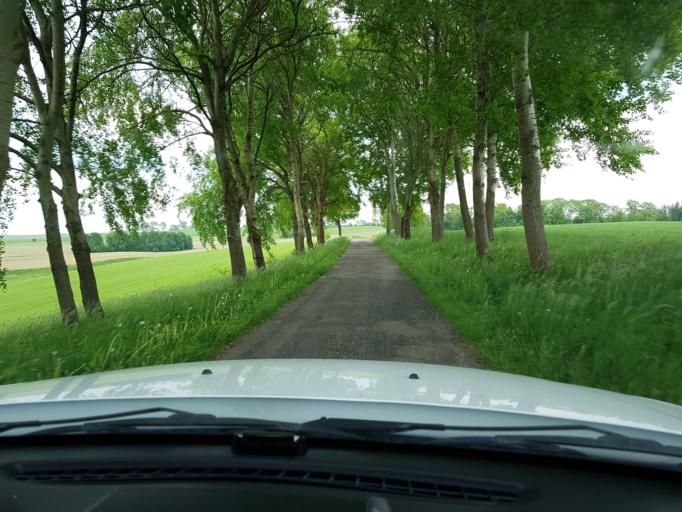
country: PL
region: West Pomeranian Voivodeship
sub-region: Powiat drawski
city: Drawsko Pomorskie
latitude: 53.5304
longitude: 15.7436
